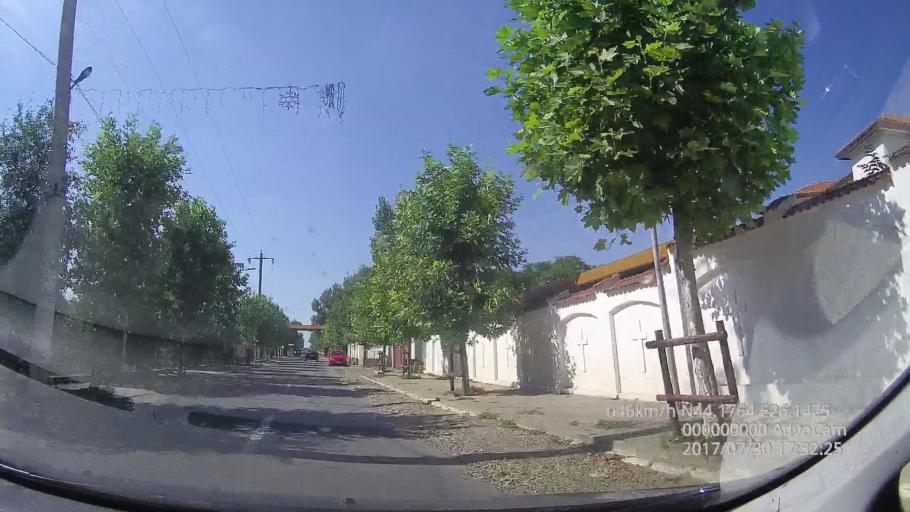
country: RO
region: Giurgiu
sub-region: Comuna Comana
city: Comana
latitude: 44.1765
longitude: 26.1424
